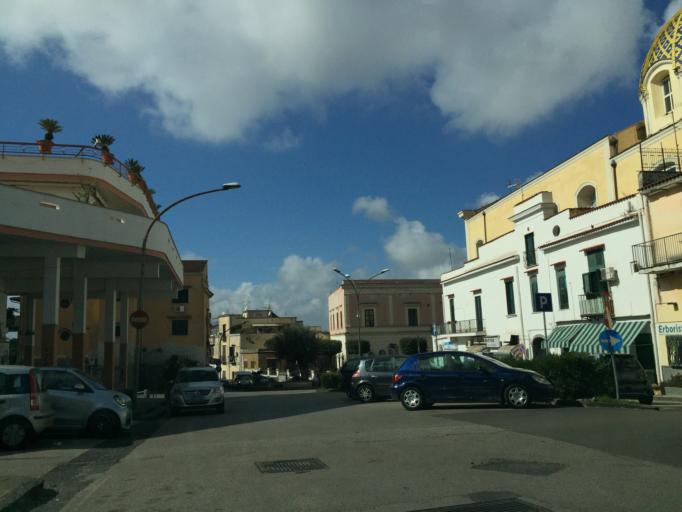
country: IT
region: Campania
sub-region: Provincia di Napoli
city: Massa di Somma
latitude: 40.8427
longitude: 14.3704
